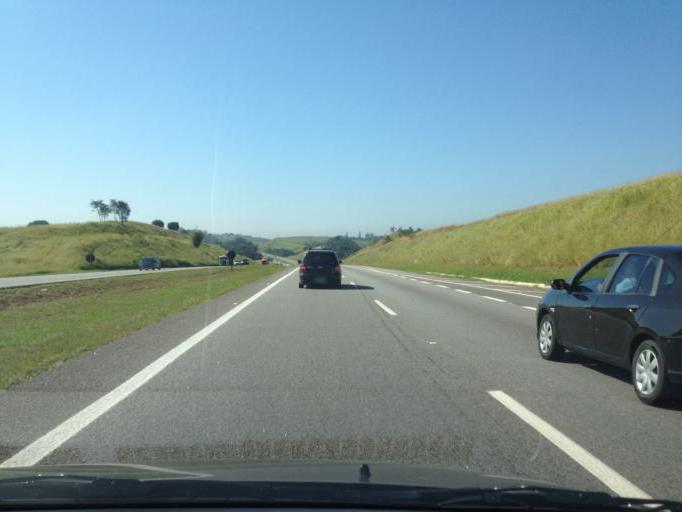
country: BR
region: Sao Paulo
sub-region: Guararema
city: Guararema
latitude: -23.3591
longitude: -46.0726
